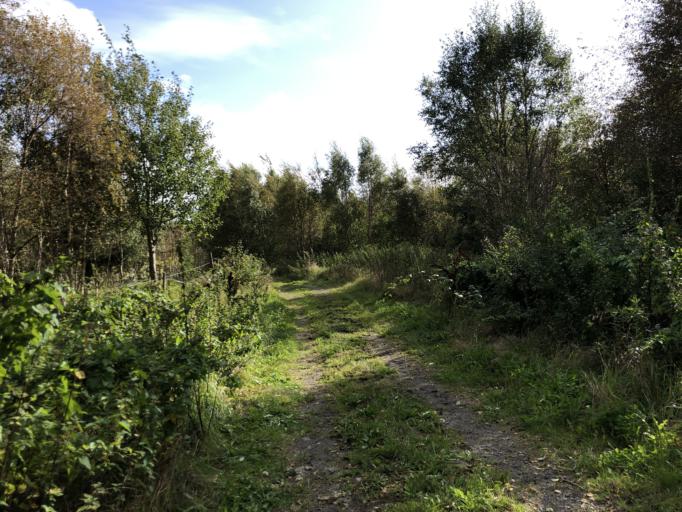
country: SE
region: Vaestra Goetaland
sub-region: Goteborg
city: Majorna
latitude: 57.7609
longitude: 11.8685
